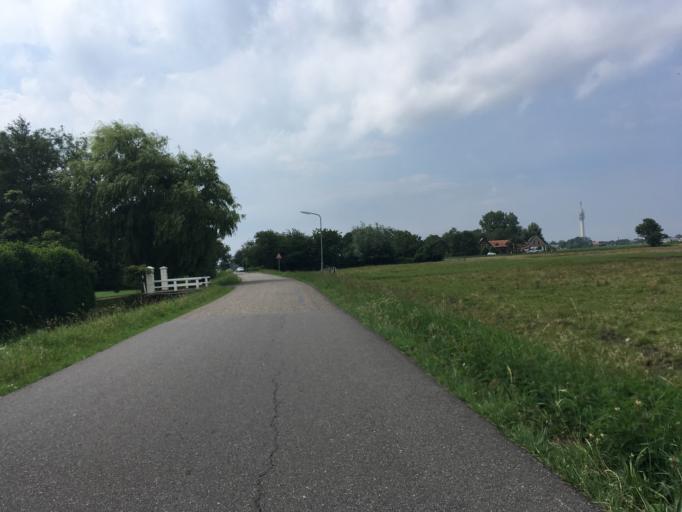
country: NL
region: North Holland
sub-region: Gemeente Haarlem
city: Haarlem
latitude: 52.3980
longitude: 4.6924
